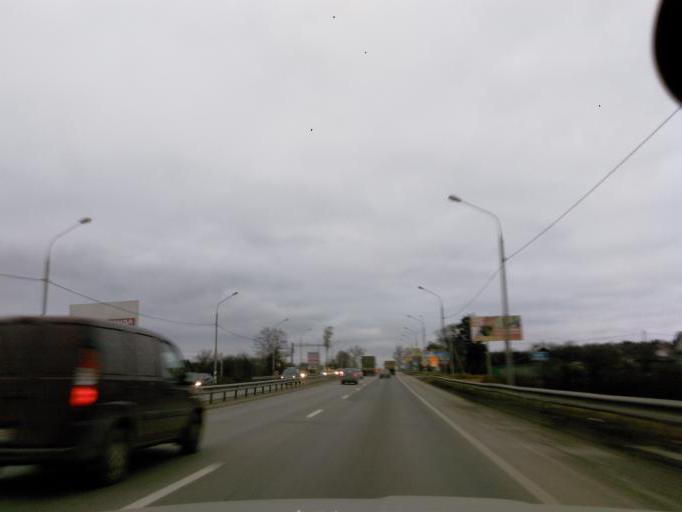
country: RU
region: Moskovskaya
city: Radumlya
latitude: 56.0556
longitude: 37.1495
